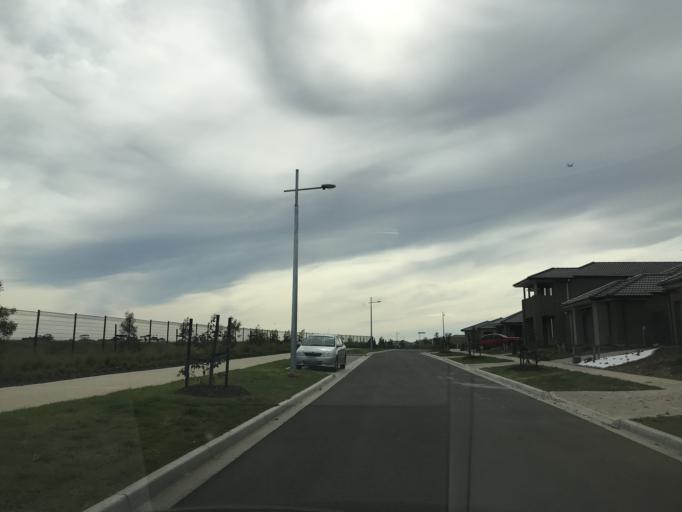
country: AU
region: Victoria
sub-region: Wyndham
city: Truganina
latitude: -37.8323
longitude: 144.7119
